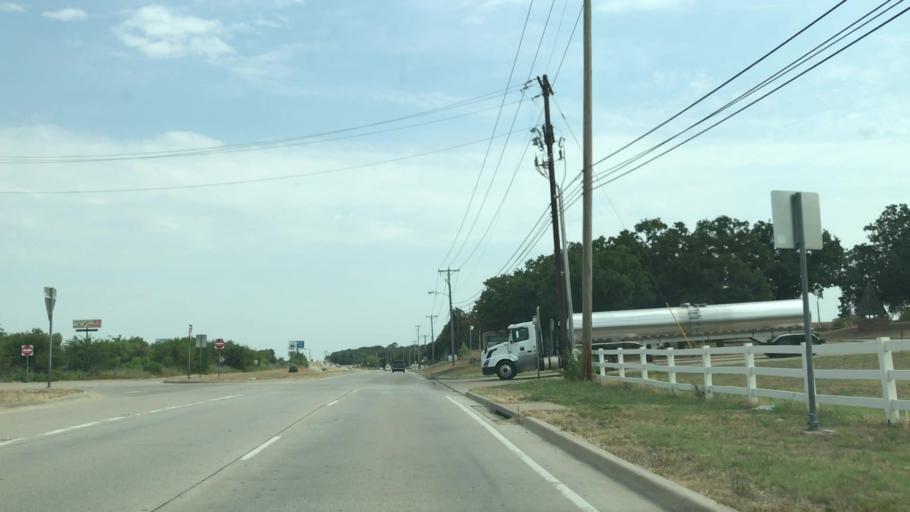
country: US
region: Texas
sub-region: Tarrant County
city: Keller
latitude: 32.9436
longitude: -97.2539
